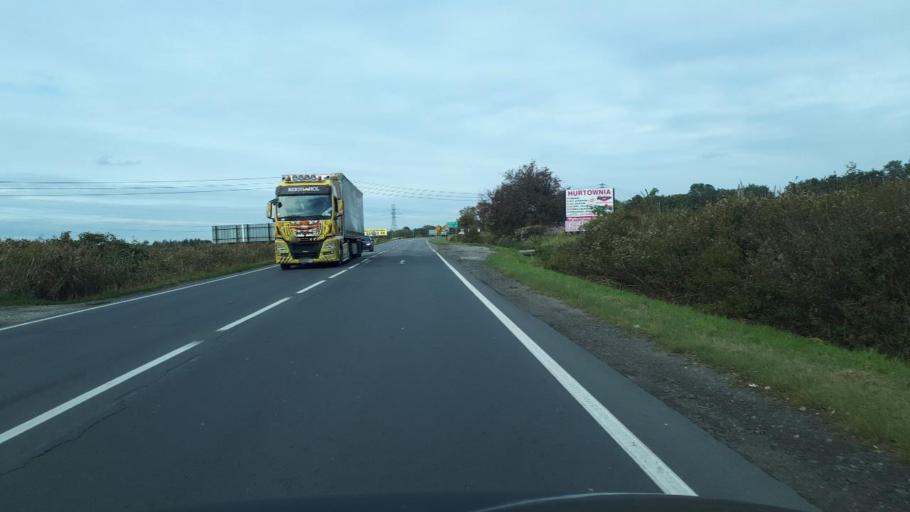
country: PL
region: Silesian Voivodeship
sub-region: Powiat gliwicki
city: Pyskowice
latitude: 50.3694
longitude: 18.6362
